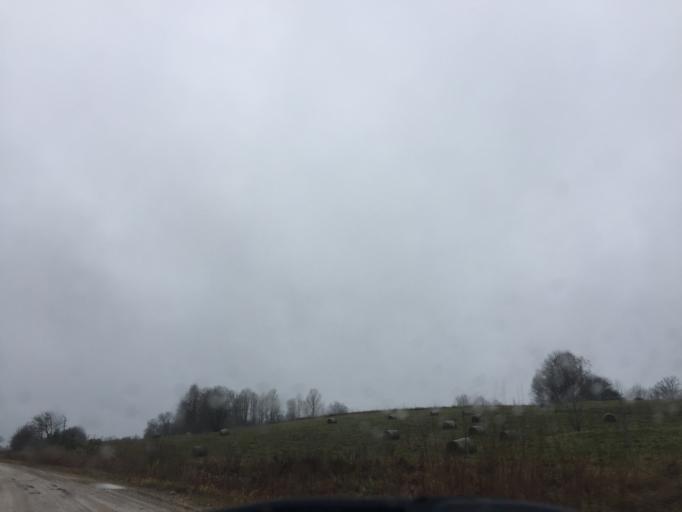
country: LV
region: Salas
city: Sala
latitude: 56.4958
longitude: 25.6838
